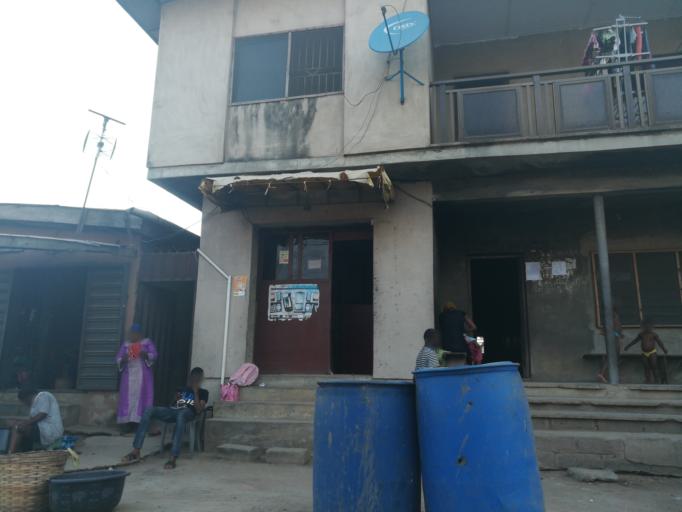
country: NG
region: Lagos
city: Ojota
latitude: 6.5888
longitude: 3.3962
